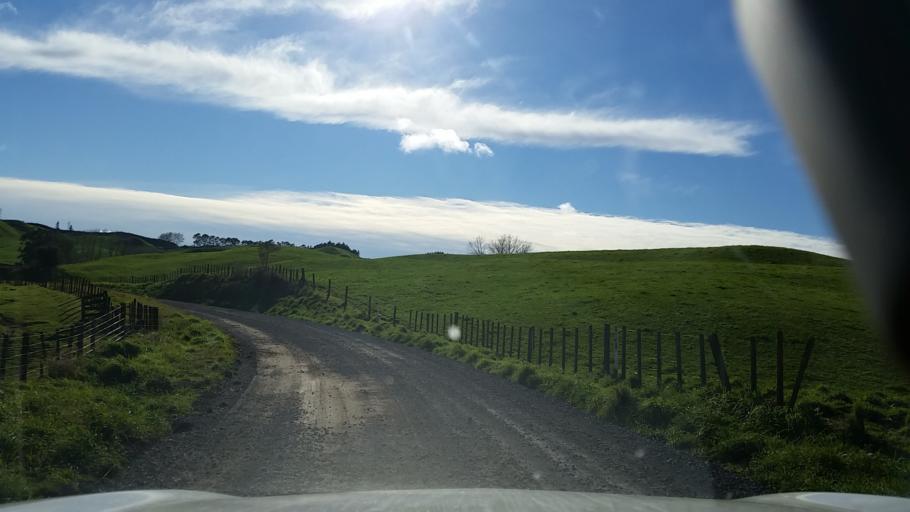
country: NZ
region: Bay of Plenty
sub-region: Rotorua District
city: Rotorua
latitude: -38.3571
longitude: 176.2322
